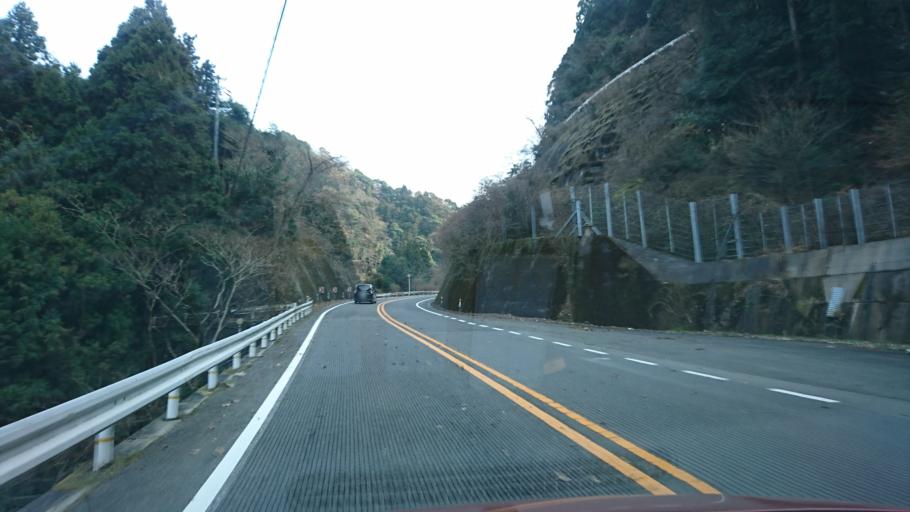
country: JP
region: Ehime
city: Hojo
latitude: 33.9603
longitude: 132.9084
